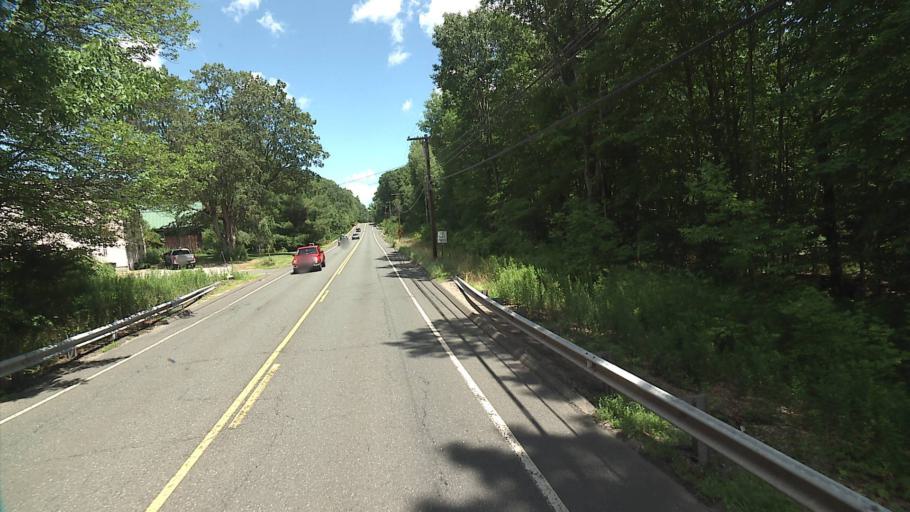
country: US
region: Connecticut
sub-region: Hartford County
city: West Simsbury
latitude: 41.9433
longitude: -72.9075
